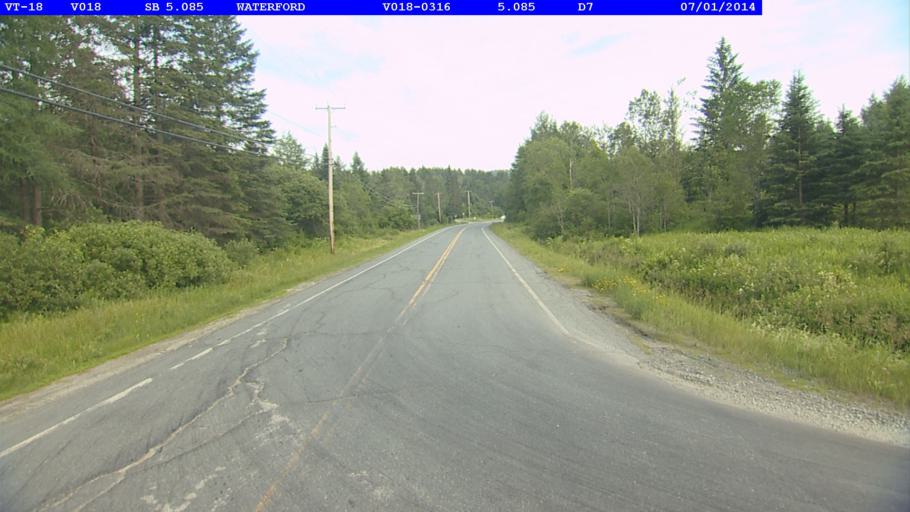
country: US
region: Vermont
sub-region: Caledonia County
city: Saint Johnsbury
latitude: 44.4044
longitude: -71.9249
